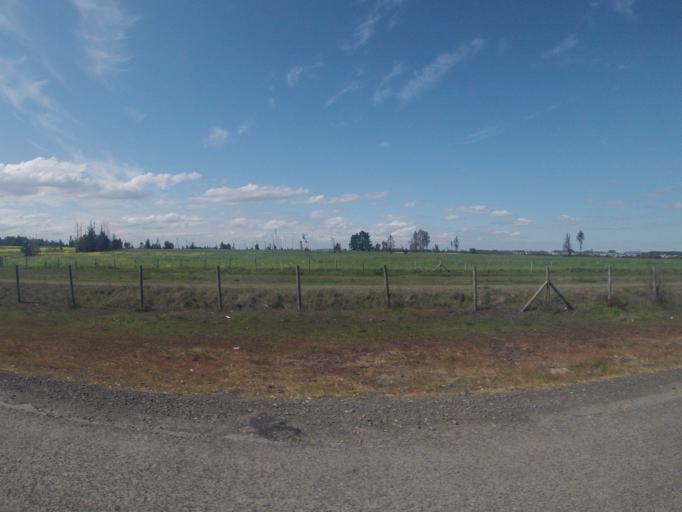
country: CL
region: Biobio
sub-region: Provincia de Biobio
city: Los Angeles
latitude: -37.4493
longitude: -72.4068
